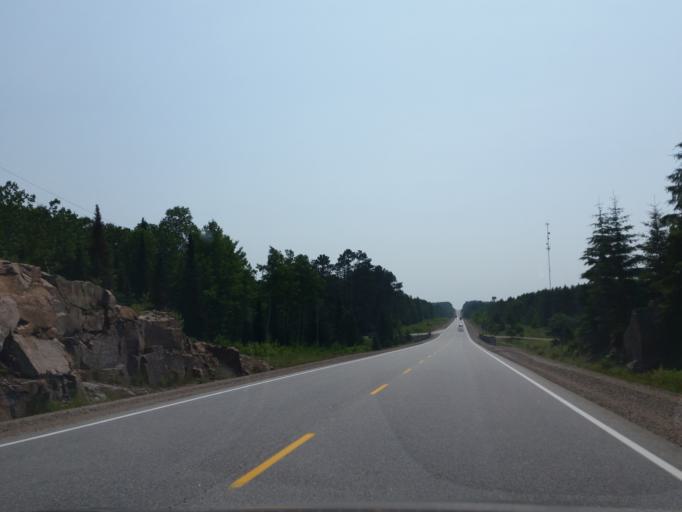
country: CA
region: Ontario
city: Mattawa
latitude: 46.2924
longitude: -78.5341
